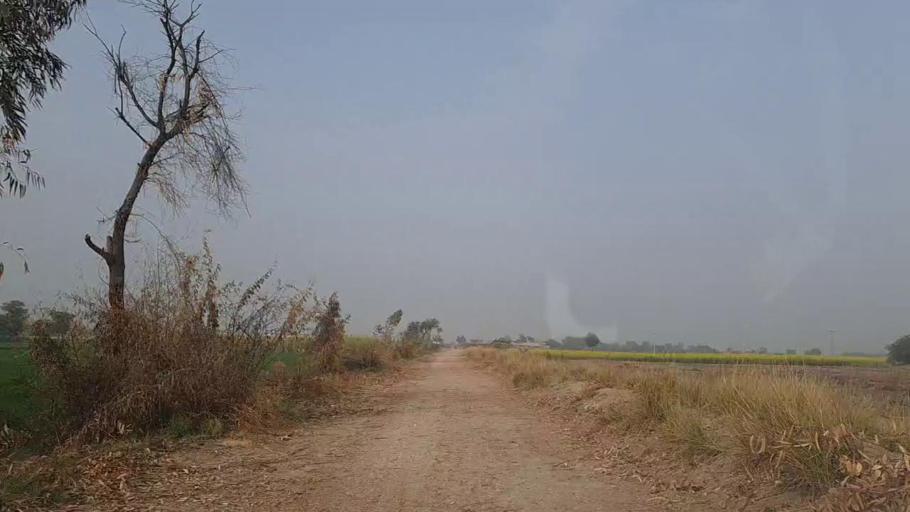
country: PK
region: Sindh
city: Sanghar
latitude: 26.1150
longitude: 68.8963
